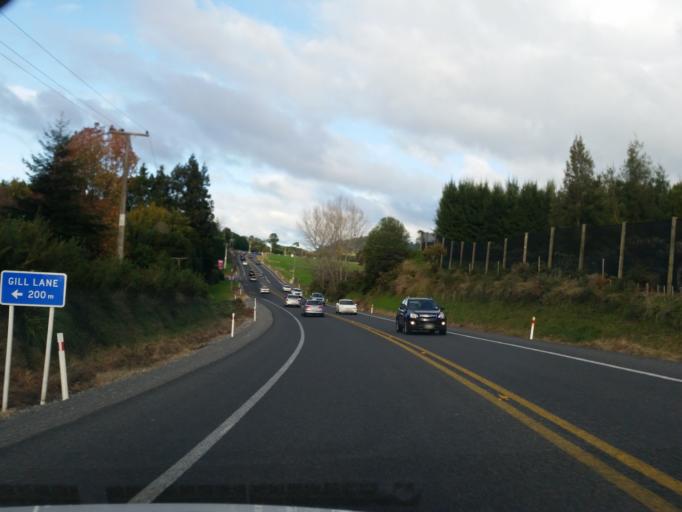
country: NZ
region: Bay of Plenty
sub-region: Tauranga City
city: Tauranga
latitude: -37.6906
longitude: 176.0422
